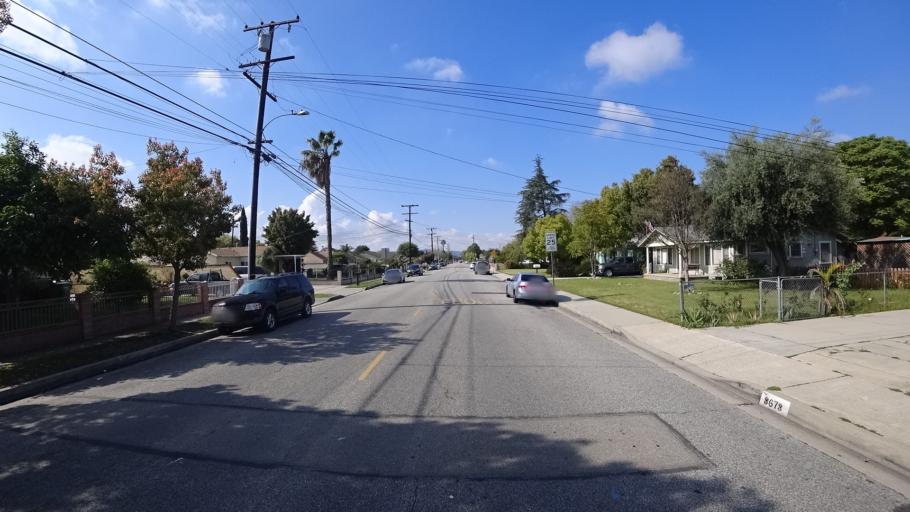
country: US
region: California
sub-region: Los Angeles County
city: Baldwin Park
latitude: 34.0807
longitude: -117.9593
